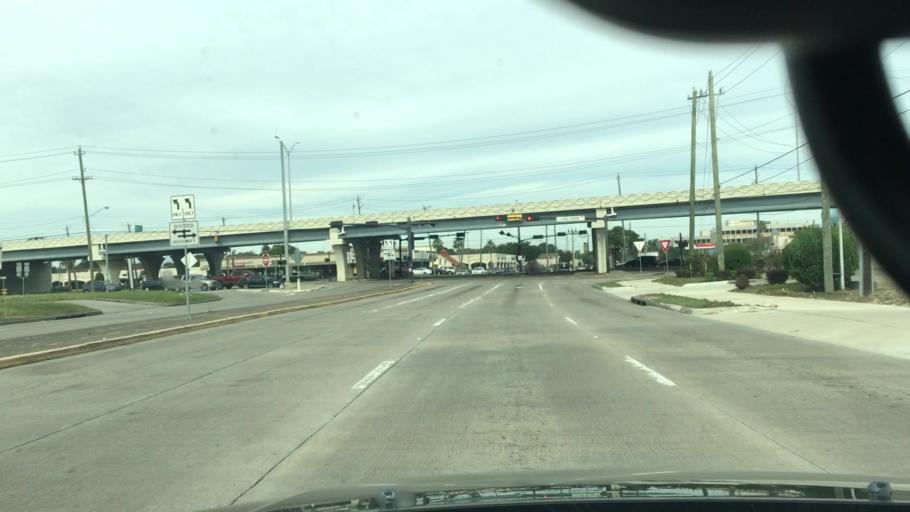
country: US
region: Texas
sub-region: Harris County
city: Nassau Bay
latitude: 29.5452
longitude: -95.1056
